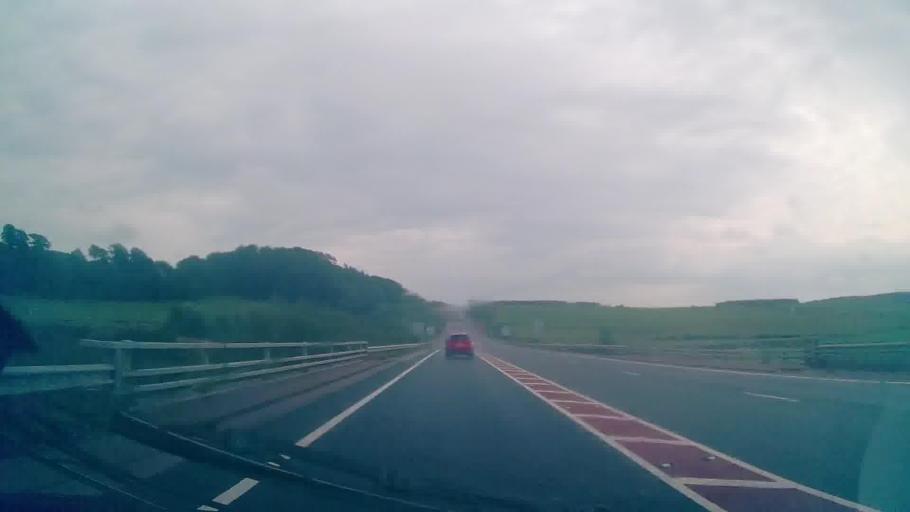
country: GB
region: Scotland
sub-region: Dumfries and Galloway
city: Lockerbie
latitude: 55.0272
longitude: -3.3867
